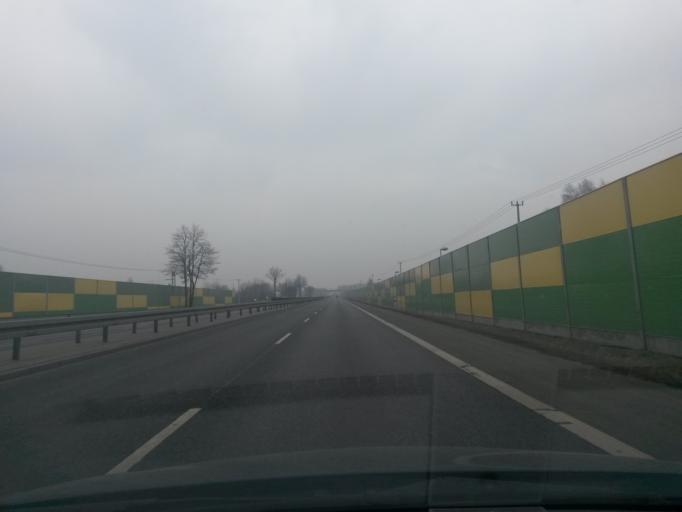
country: PL
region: Masovian Voivodeship
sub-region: Powiat legionowski
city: Bialobrzegi
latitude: 52.4776
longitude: 21.0349
